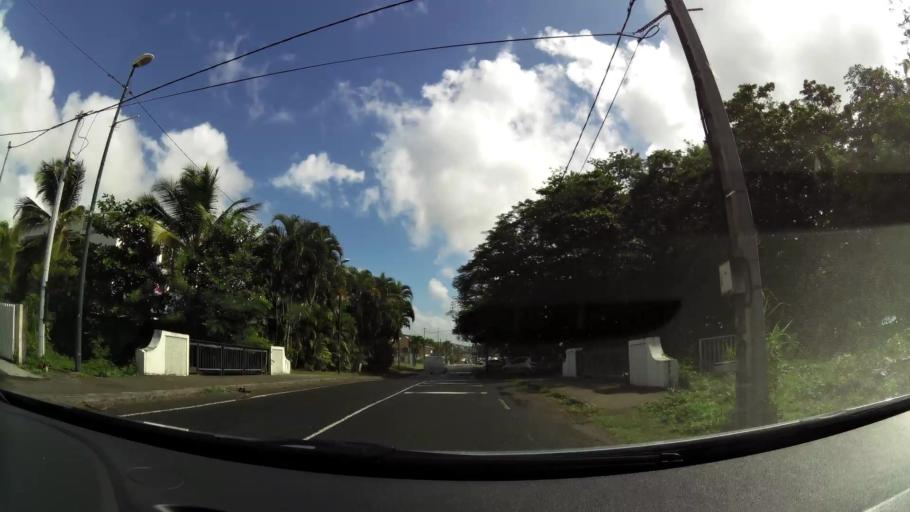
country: MQ
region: Martinique
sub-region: Martinique
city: Les Trois-Ilets
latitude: 14.4782
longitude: -61.0317
